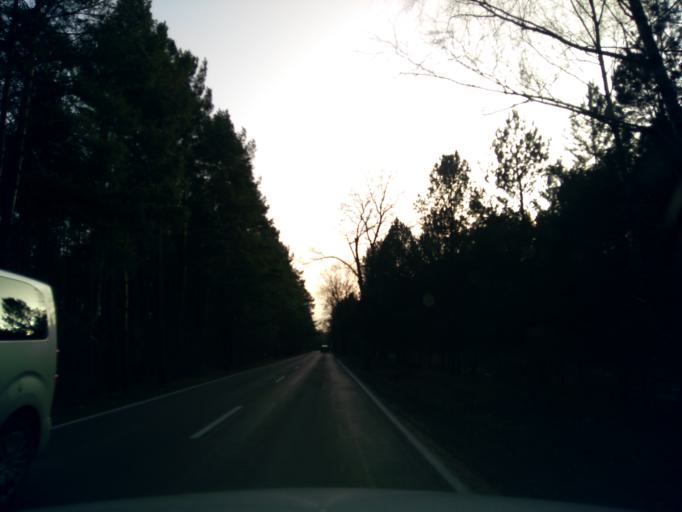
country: DE
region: Brandenburg
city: Birkenwerder
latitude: 52.7181
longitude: 13.3670
